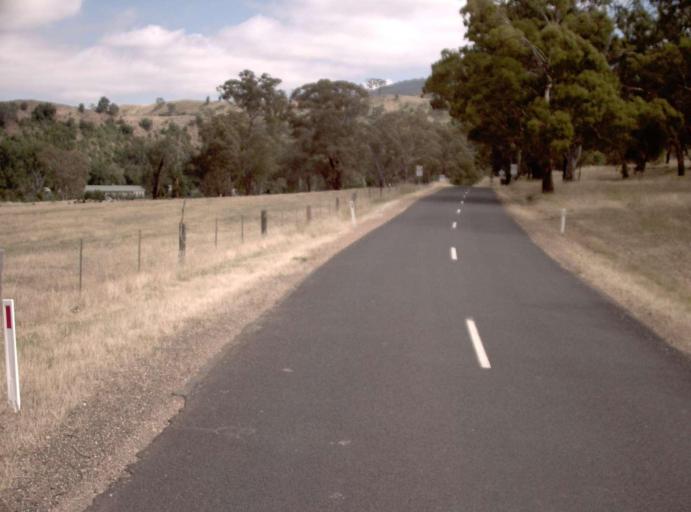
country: AU
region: Victoria
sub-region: Wellington
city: Heyfield
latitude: -37.6336
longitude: 146.6238
